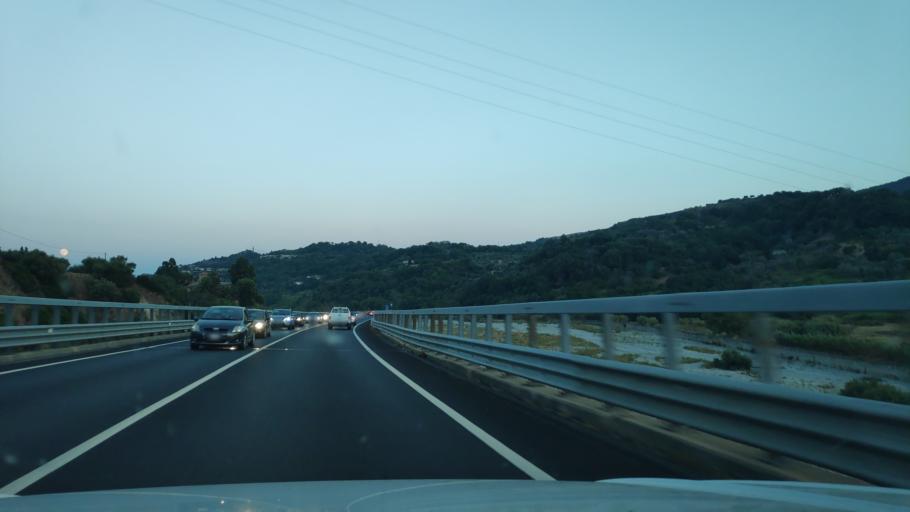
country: IT
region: Calabria
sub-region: Provincia di Reggio Calabria
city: Grotteria
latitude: 38.3484
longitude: 16.2557
